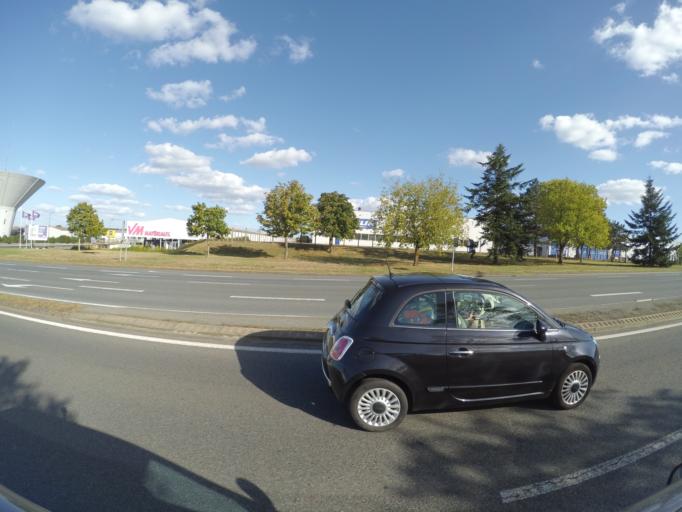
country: FR
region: Pays de la Loire
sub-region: Departement de Maine-et-Loire
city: Mazieres-en-Mauges
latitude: 47.0661
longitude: -0.8430
